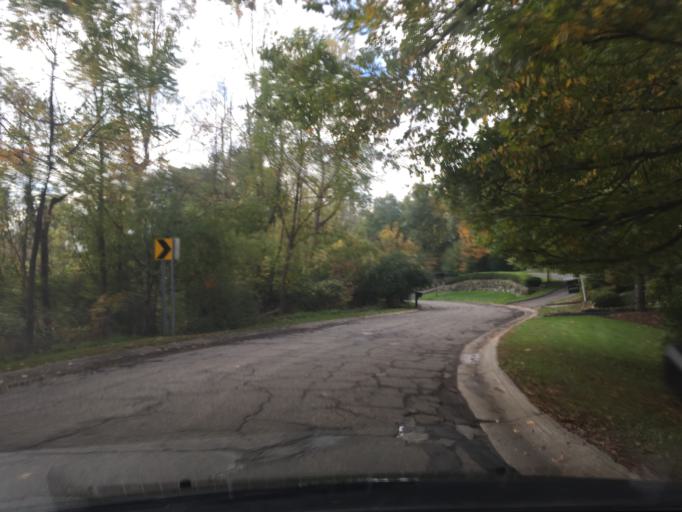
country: US
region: Michigan
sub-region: Oakland County
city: Sylvan Lake
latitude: 42.5912
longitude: -83.3178
